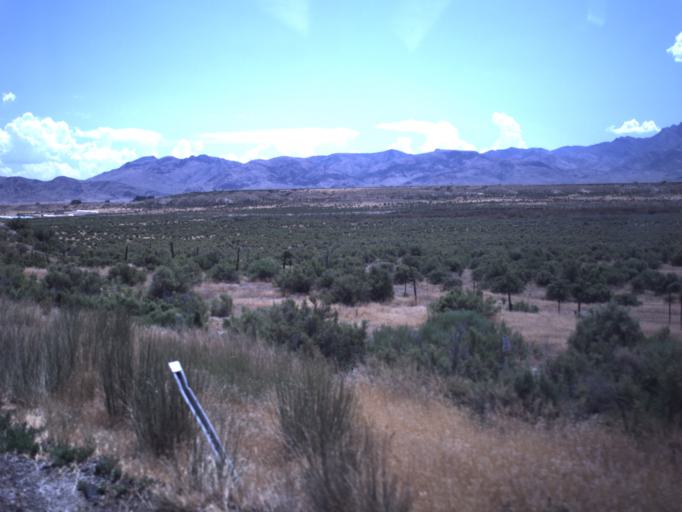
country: US
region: Utah
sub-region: Millard County
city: Delta
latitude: 39.5266
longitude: -112.3573
